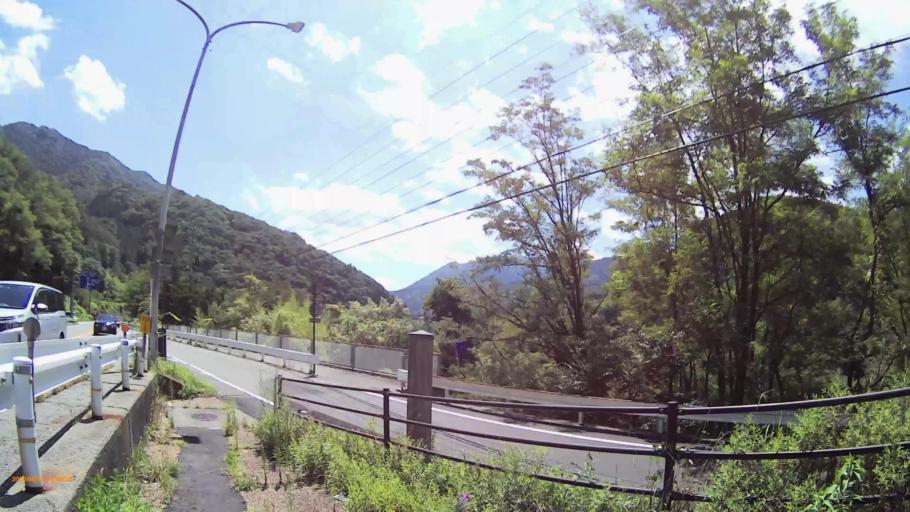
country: JP
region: Nagano
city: Ina
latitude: 35.8297
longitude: 137.6822
